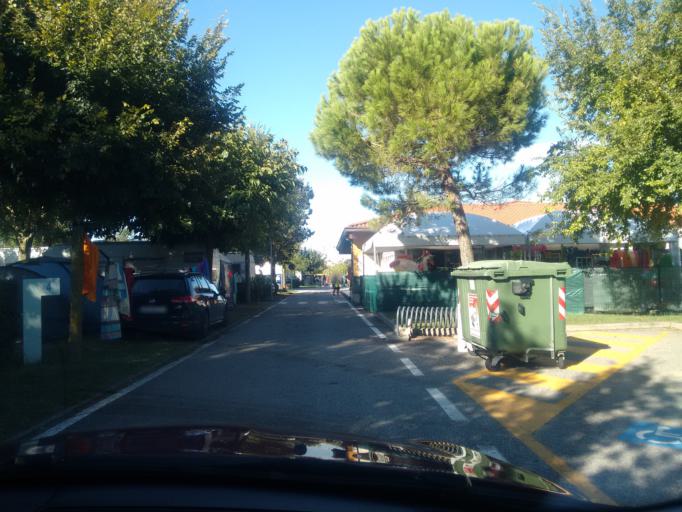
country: IT
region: Veneto
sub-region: Provincia di Venezia
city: Caorle
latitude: 45.5781
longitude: 12.8285
